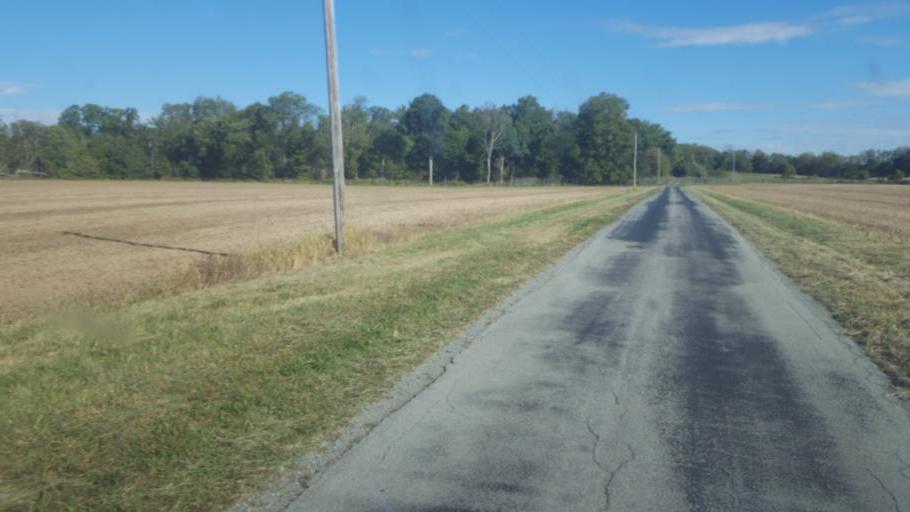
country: US
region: Ohio
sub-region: Wyandot County
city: Upper Sandusky
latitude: 40.7555
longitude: -83.2069
